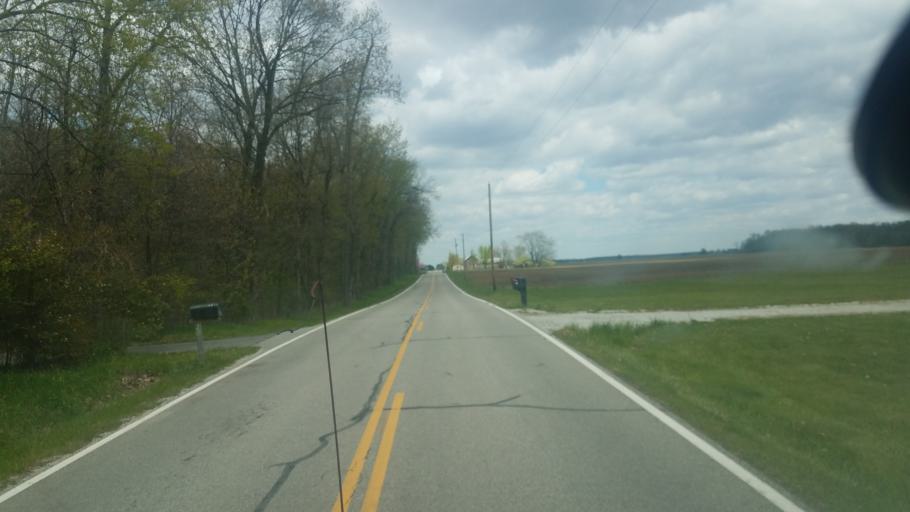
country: US
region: Ohio
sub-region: Marion County
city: Marion
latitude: 40.7035
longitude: -83.0923
